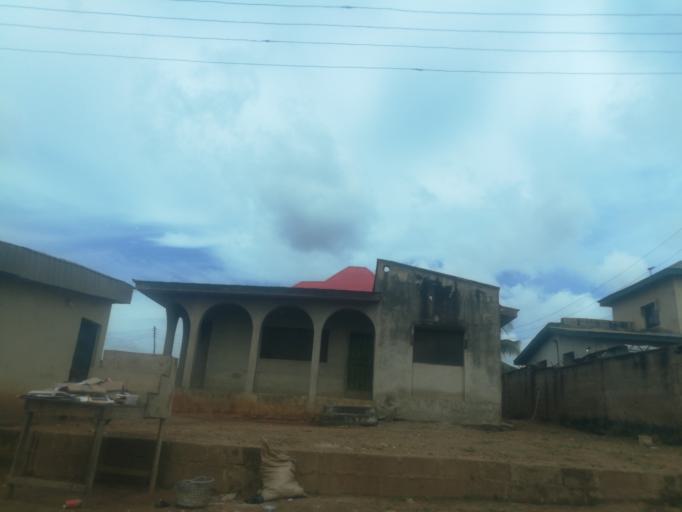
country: NG
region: Oyo
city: Ibadan
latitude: 7.3663
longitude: 3.9715
